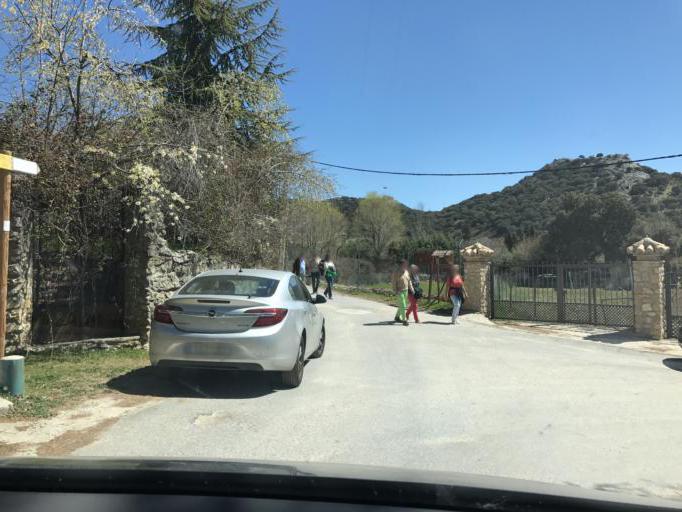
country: ES
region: Andalusia
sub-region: Provincia de Granada
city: Iznalloz
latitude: 37.3224
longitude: -3.4530
